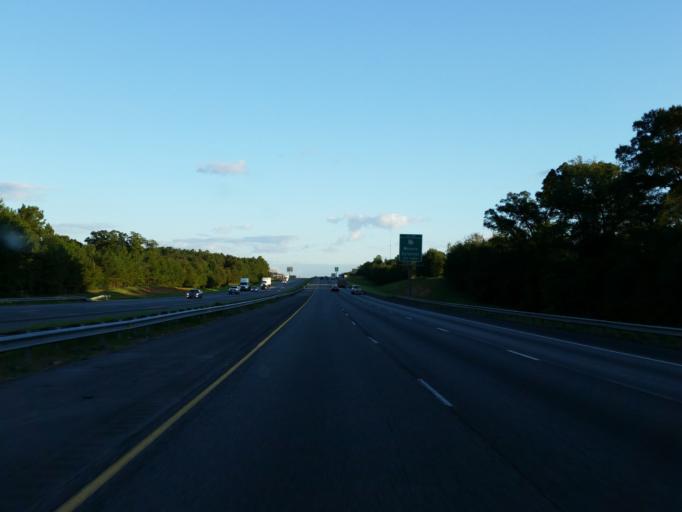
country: US
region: Georgia
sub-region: Crisp County
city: Cordele
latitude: 31.9237
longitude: -83.7447
